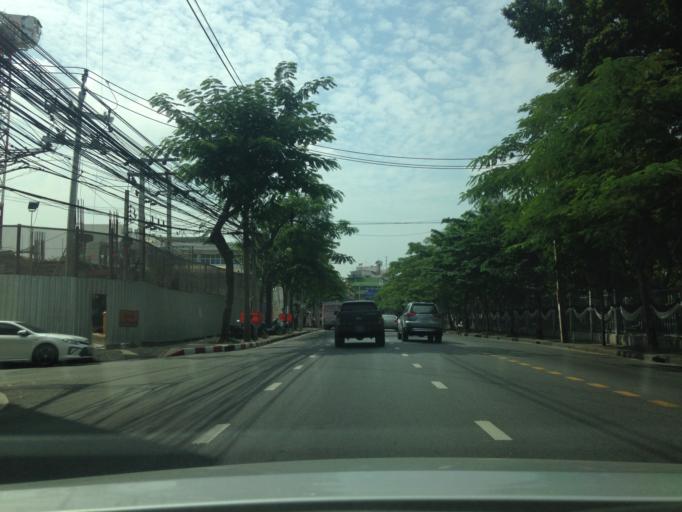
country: TH
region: Bangkok
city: Phra Nakhon
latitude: 13.7725
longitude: 100.5057
